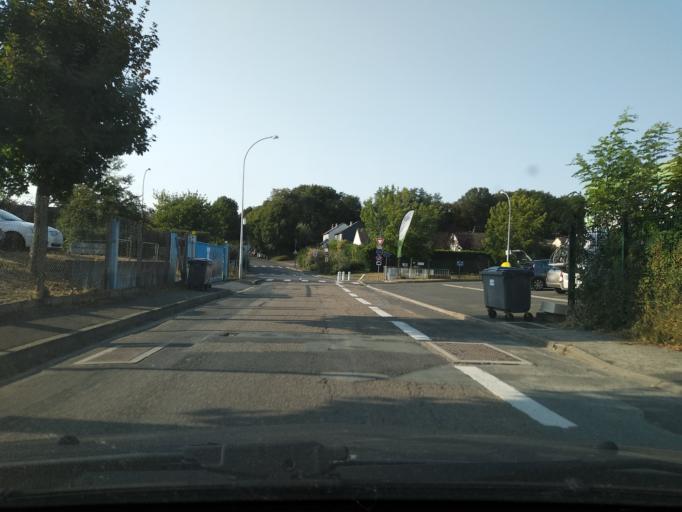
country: FR
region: Centre
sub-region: Departement d'Indre-et-Loire
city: Saint-Cyr-sur-Loire
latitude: 47.4315
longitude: 0.6830
